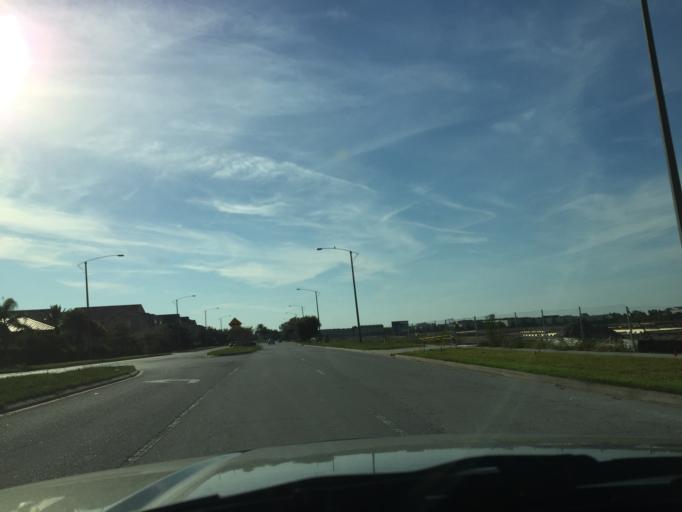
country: US
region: Florida
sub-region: Orange County
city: Oak Ridge
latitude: 28.4943
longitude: -81.4200
